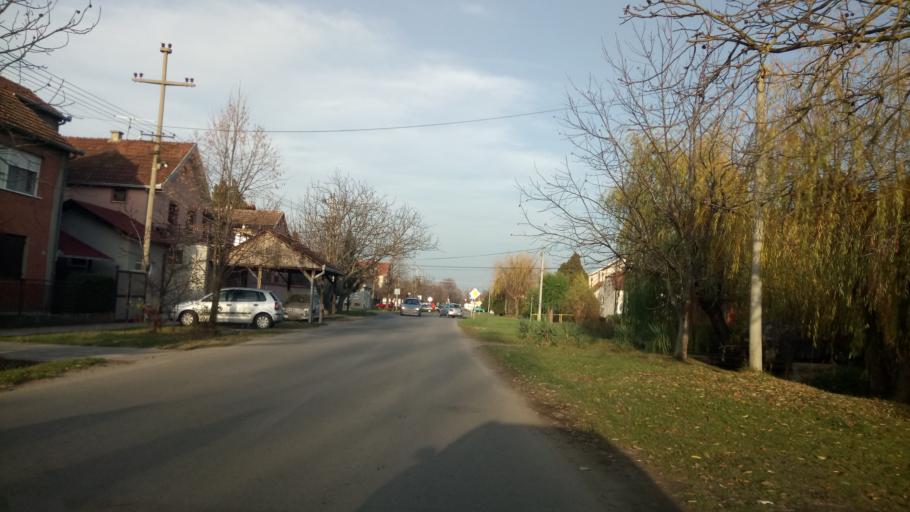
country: RS
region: Autonomna Pokrajina Vojvodina
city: Nova Pazova
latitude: 44.9380
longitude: 20.2231
